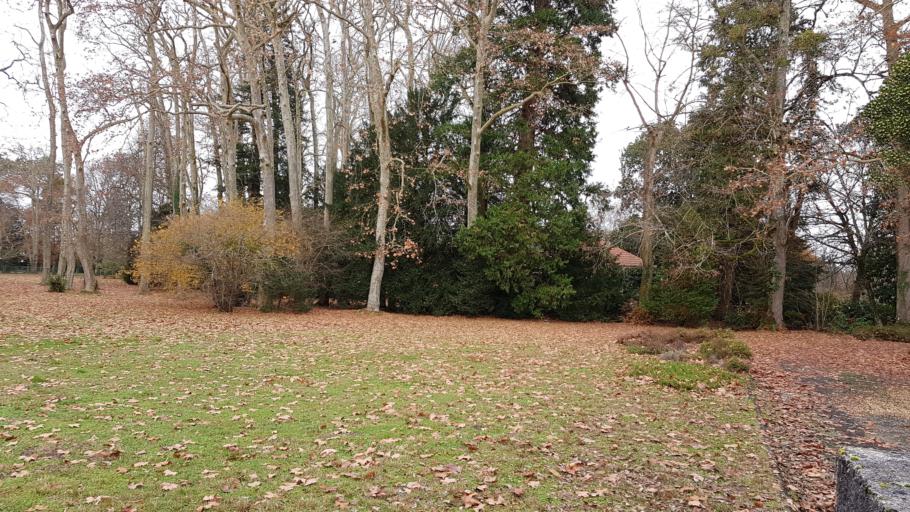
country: FR
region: Aquitaine
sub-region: Departement des Landes
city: Saint-Paul-les-Dax
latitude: 43.7422
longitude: -1.0533
